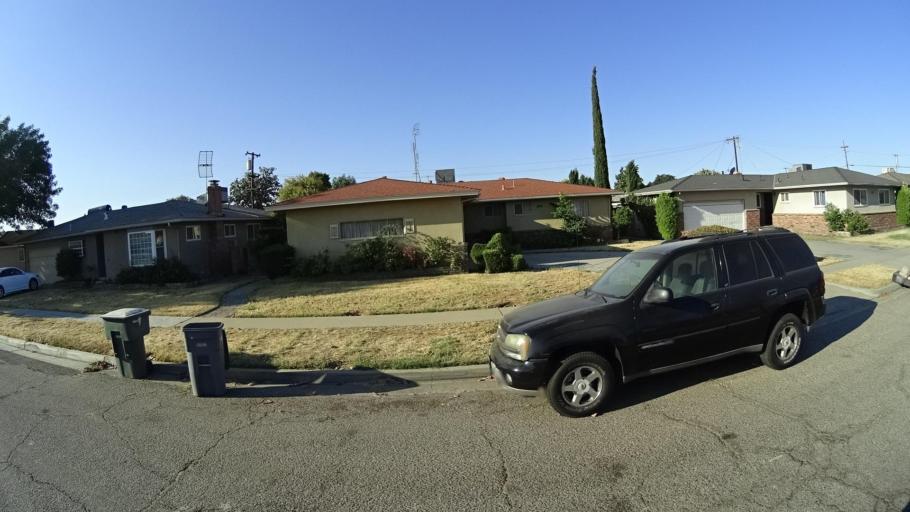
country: US
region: California
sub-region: Fresno County
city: Fresno
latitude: 36.7768
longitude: -119.8337
